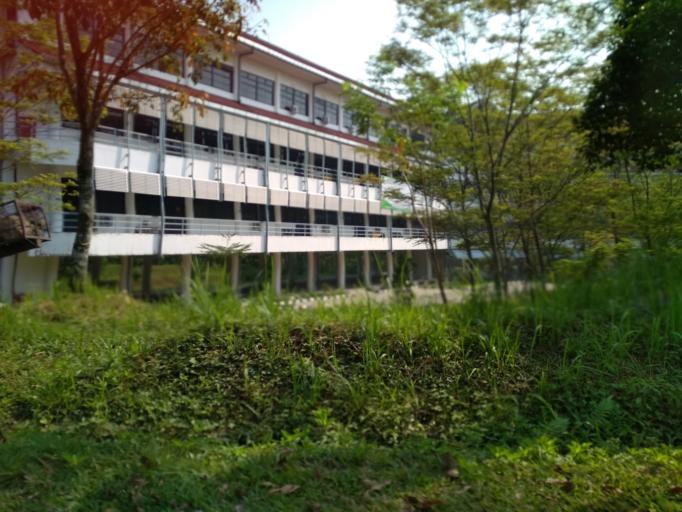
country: ID
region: West Java
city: Ciampea
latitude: -6.5602
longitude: 106.7227
